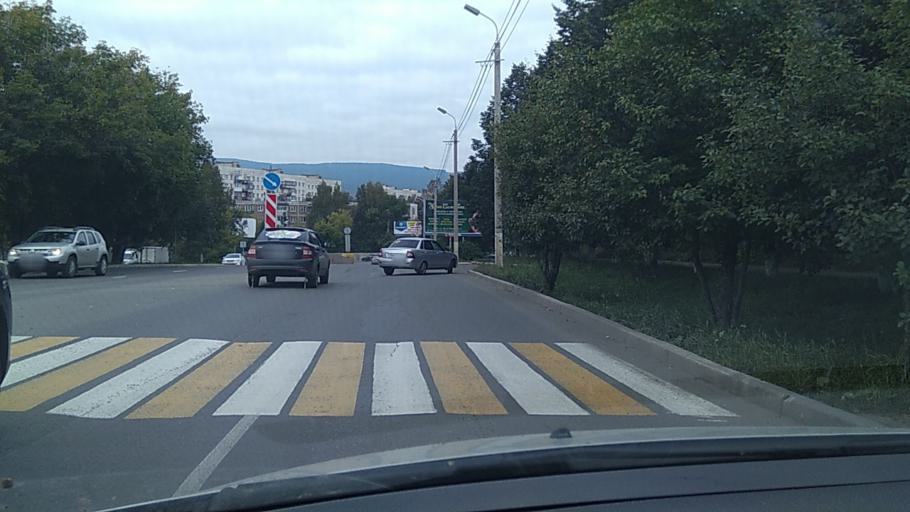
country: RU
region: Chelyabinsk
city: Zlatoust
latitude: 55.1139
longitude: 59.7111
